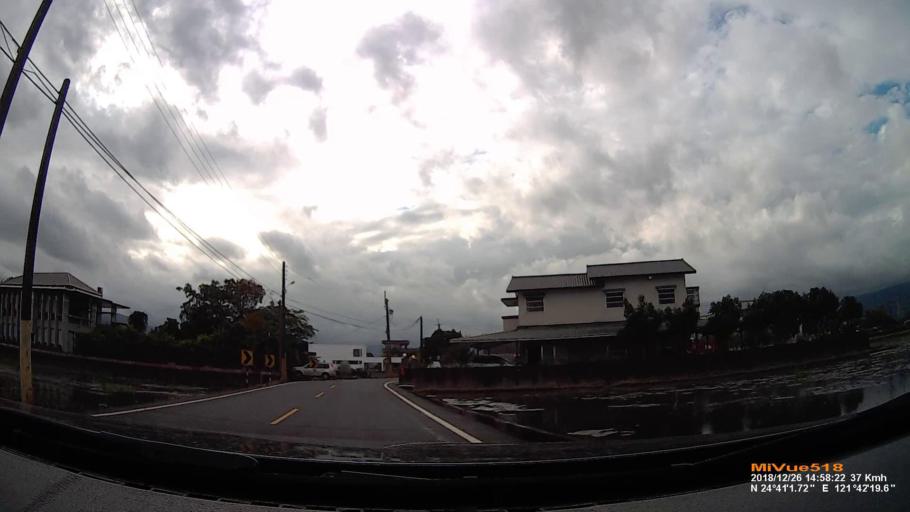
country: TW
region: Taiwan
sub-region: Yilan
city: Yilan
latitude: 24.6778
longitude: 121.6788
